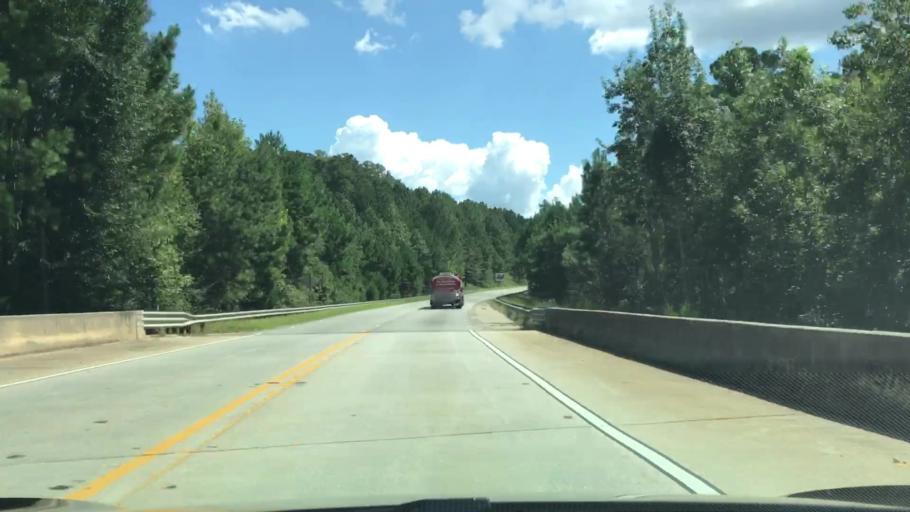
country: US
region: Georgia
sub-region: Oconee County
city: Watkinsville
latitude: 33.7201
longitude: -83.2947
